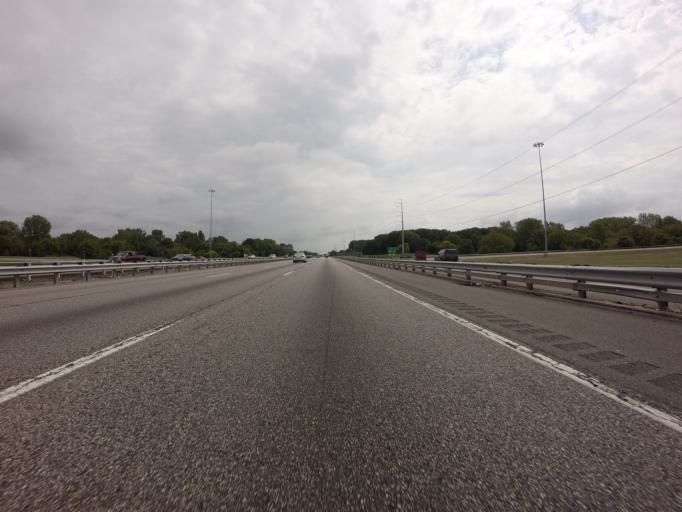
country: US
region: Pennsylvania
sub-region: Delaware County
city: Prospect Park
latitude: 39.8709
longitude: -75.3008
